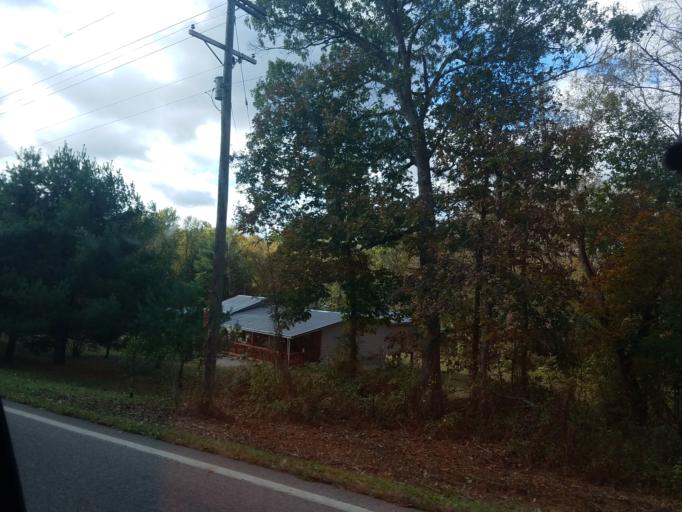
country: US
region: Ohio
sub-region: Vinton County
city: McArthur
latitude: 39.1976
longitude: -82.4805
